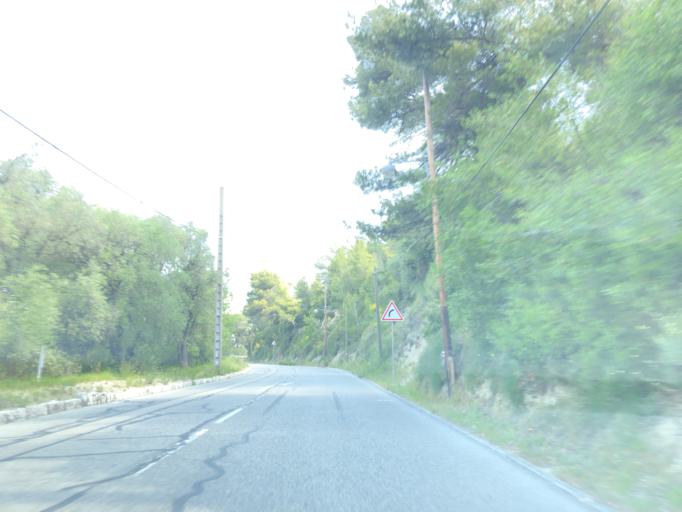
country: FR
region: Provence-Alpes-Cote d'Azur
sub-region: Departement des Alpes-Maritimes
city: Saint-Andre-de-la-Roche
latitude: 43.7292
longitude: 7.2957
